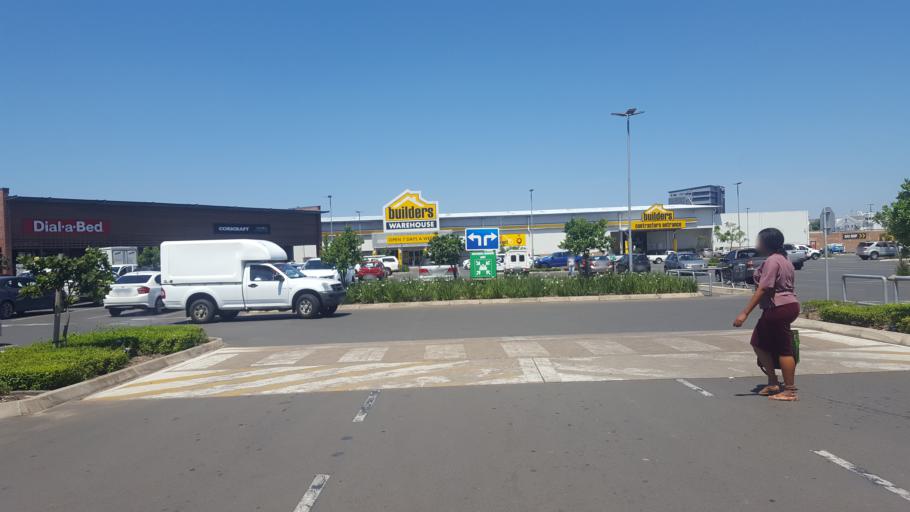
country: ZA
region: KwaZulu-Natal
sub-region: uThungulu District Municipality
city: Richards Bay
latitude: -28.7469
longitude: 32.0507
